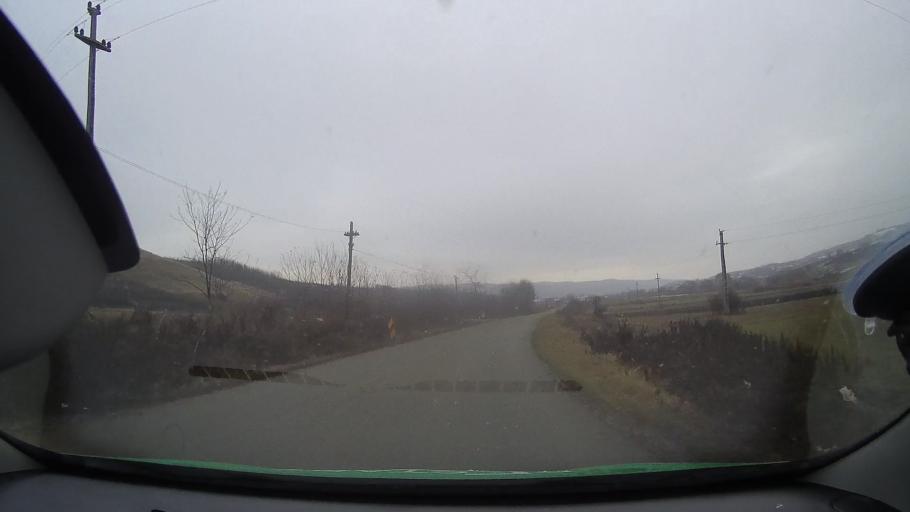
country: RO
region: Alba
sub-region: Comuna Farau
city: Farau
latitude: 46.3385
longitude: 23.9857
